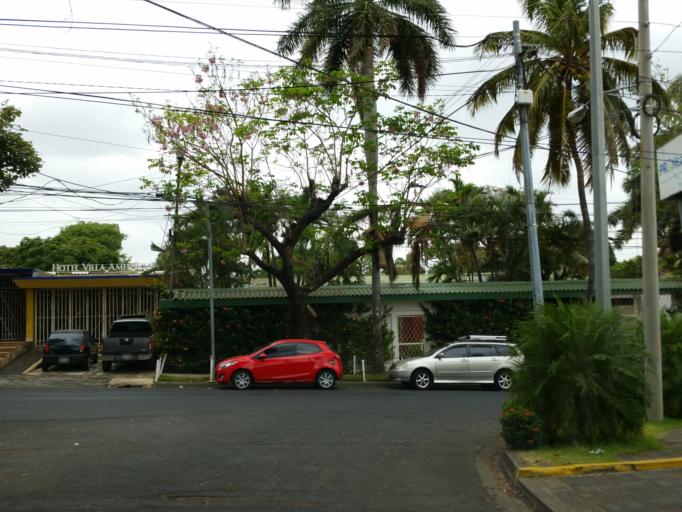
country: NI
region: Managua
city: Managua
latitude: 12.1204
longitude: -86.2631
